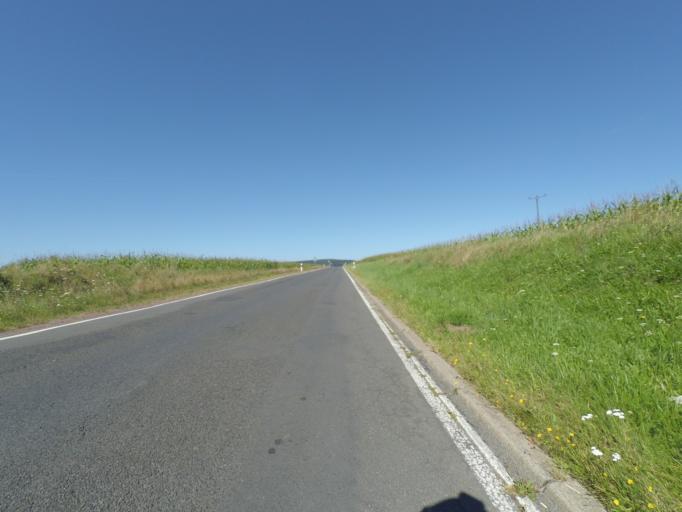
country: DE
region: Rheinland-Pfalz
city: Grosslittgen
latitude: 50.0282
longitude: 6.8158
